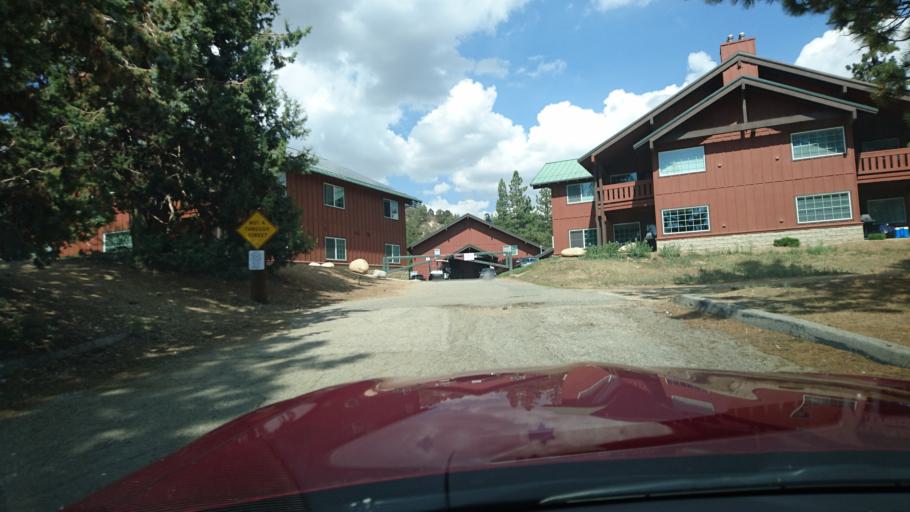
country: US
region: California
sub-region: San Bernardino County
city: Big Bear Lake
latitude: 34.2524
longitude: -116.8827
